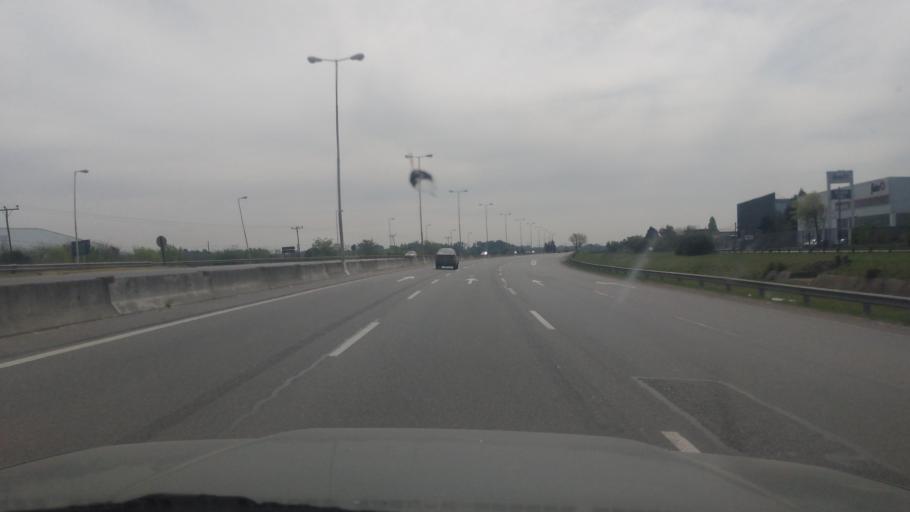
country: AR
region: Buenos Aires
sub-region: Partido de Pilar
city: Pilar
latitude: -34.4180
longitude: -59.0031
